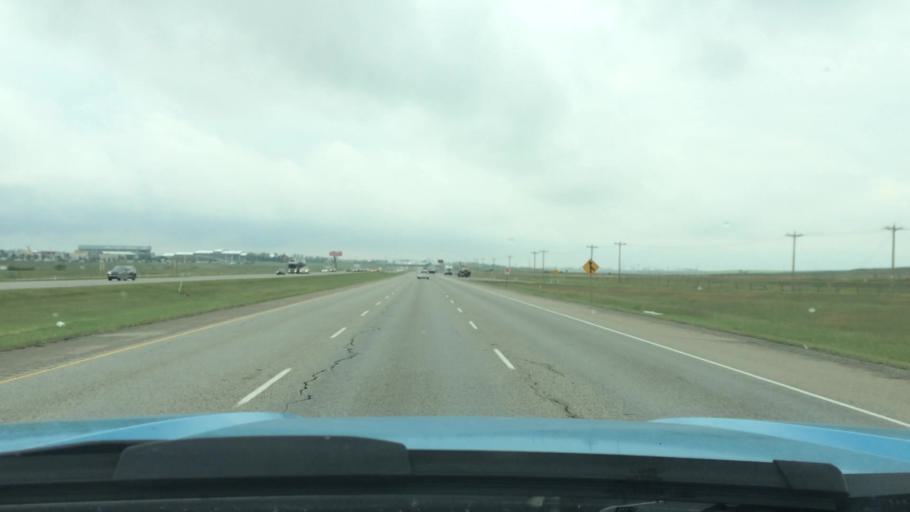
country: CA
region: Alberta
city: Airdrie
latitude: 51.2108
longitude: -114.0017
